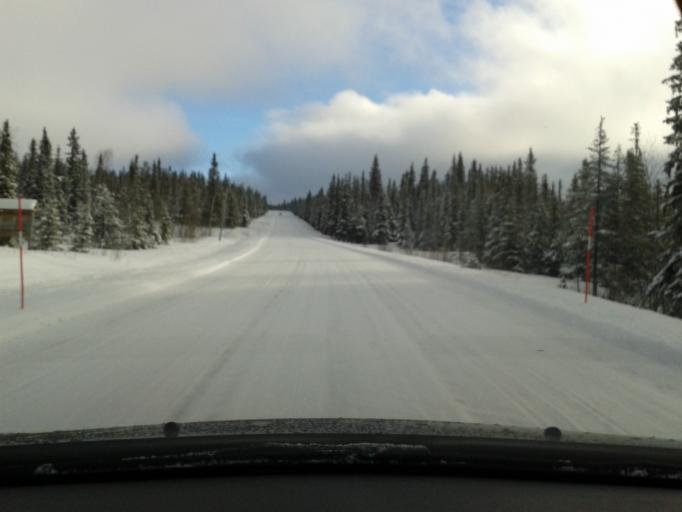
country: SE
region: Vaesterbotten
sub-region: Vilhelmina Kommun
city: Sjoberg
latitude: 65.2511
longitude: 15.6211
